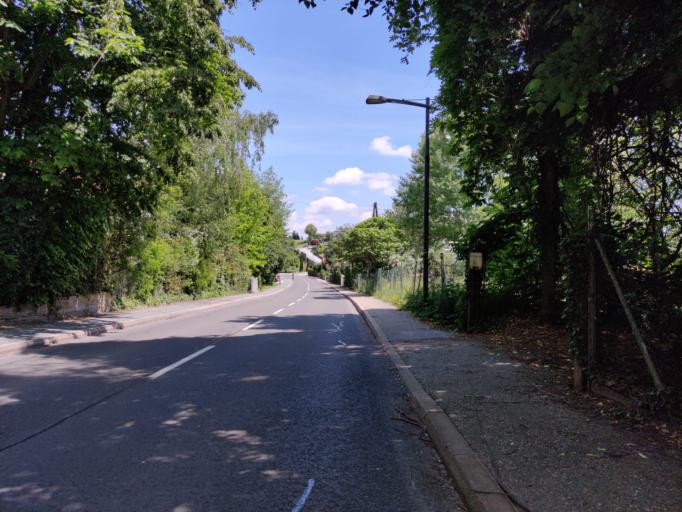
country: AT
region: Styria
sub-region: Politischer Bezirk Graz-Umgebung
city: Nestelbach bei Graz
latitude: 47.0700
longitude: 15.5900
